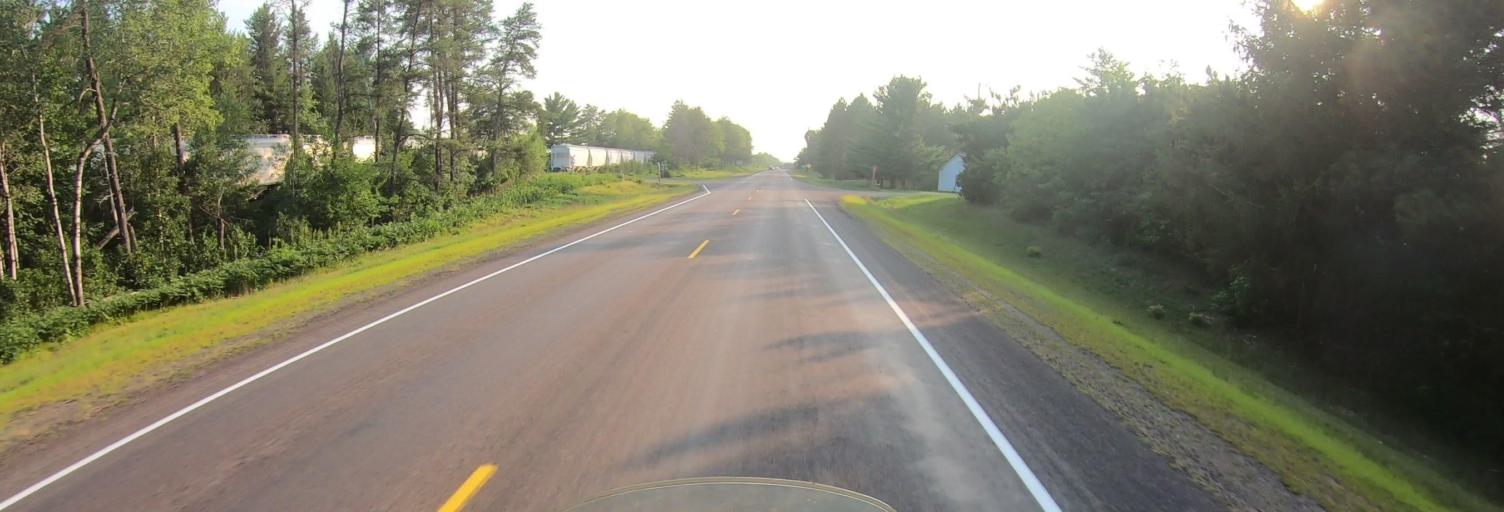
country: US
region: Wisconsin
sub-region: Washburn County
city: Spooner
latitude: 45.9129
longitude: -91.7529
